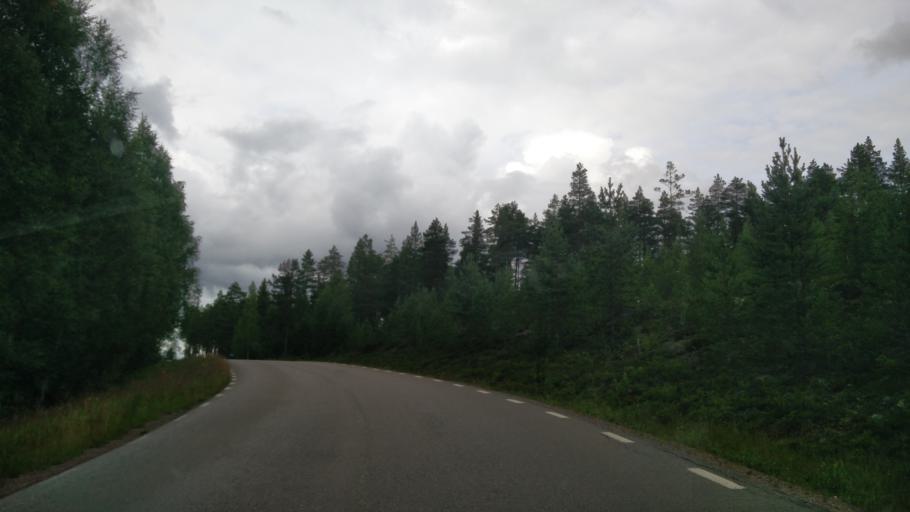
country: NO
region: Hedmark
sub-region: Trysil
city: Innbygda
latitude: 61.1602
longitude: 12.8216
